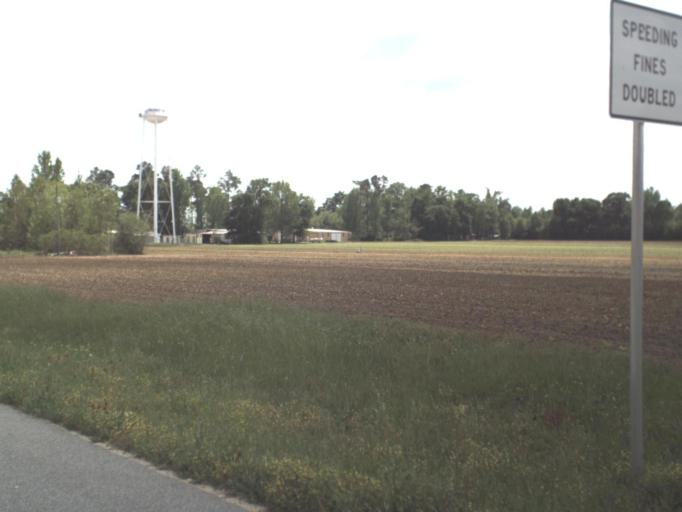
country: US
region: Alabama
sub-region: Escambia County
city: Atmore
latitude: 30.8982
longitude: -87.4777
